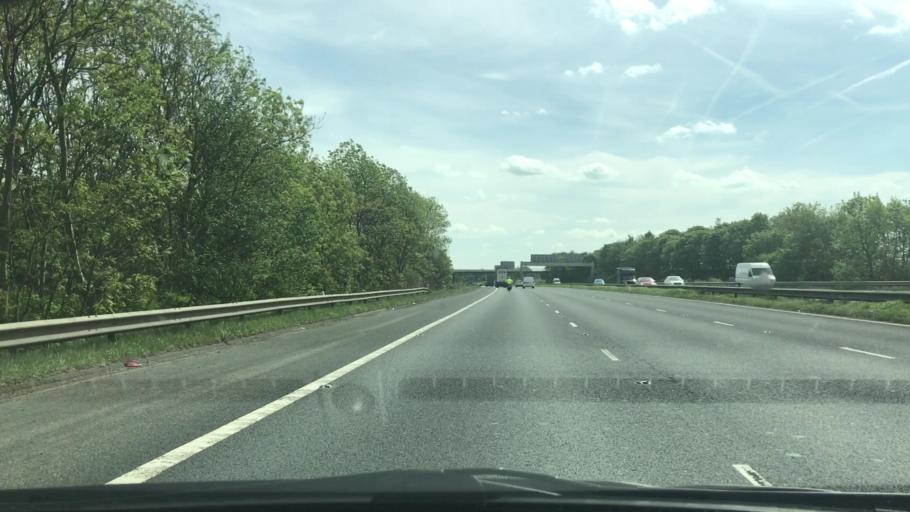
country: GB
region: England
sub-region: City and Borough of Wakefield
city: Knottingley
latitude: 53.6949
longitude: -1.2633
